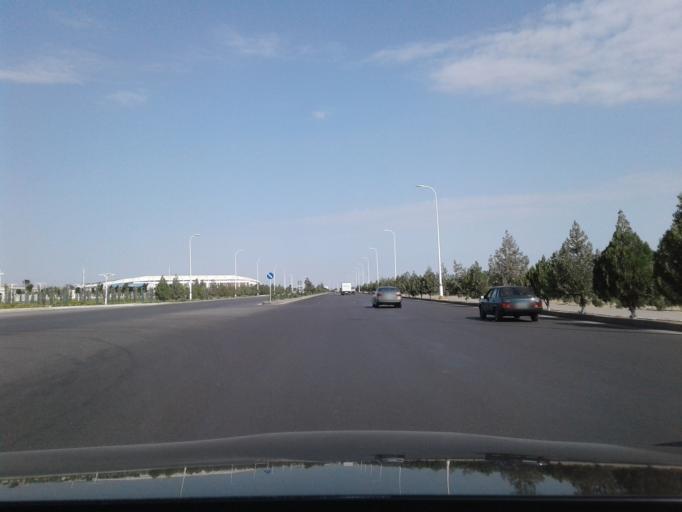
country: TM
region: Ahal
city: Abadan
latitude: 38.0439
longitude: 58.2048
